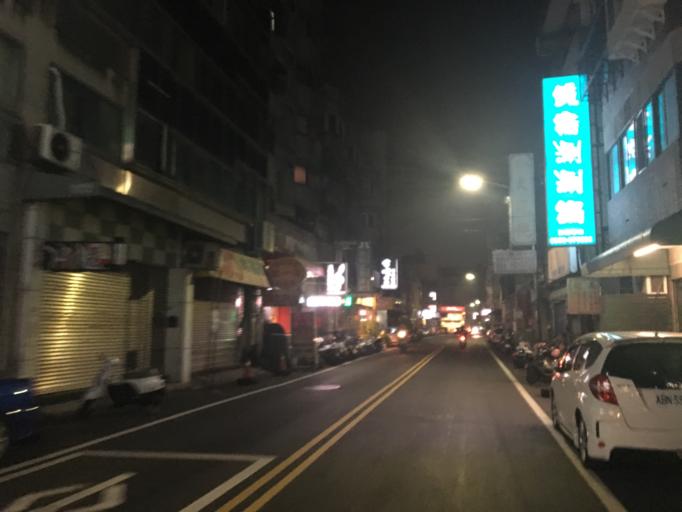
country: TW
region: Taiwan
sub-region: Hsinchu
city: Hsinchu
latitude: 24.8176
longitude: 120.9720
